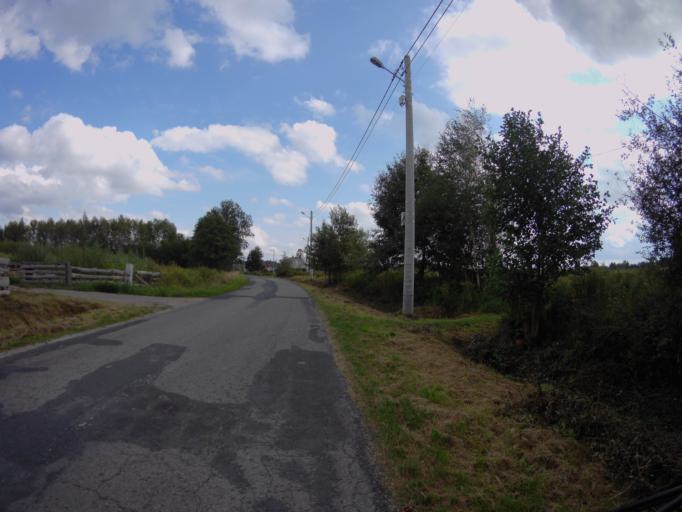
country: PL
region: Subcarpathian Voivodeship
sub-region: Powiat lezajski
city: Brzoza Krolewska
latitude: 50.2440
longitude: 22.3407
